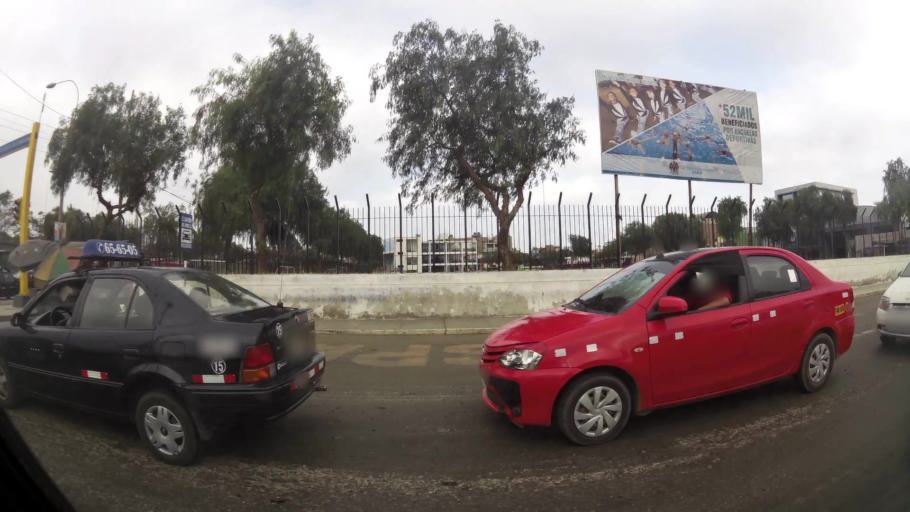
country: PE
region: La Libertad
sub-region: Provincia de Trujillo
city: Trujillo
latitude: -8.0959
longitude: -79.0194
